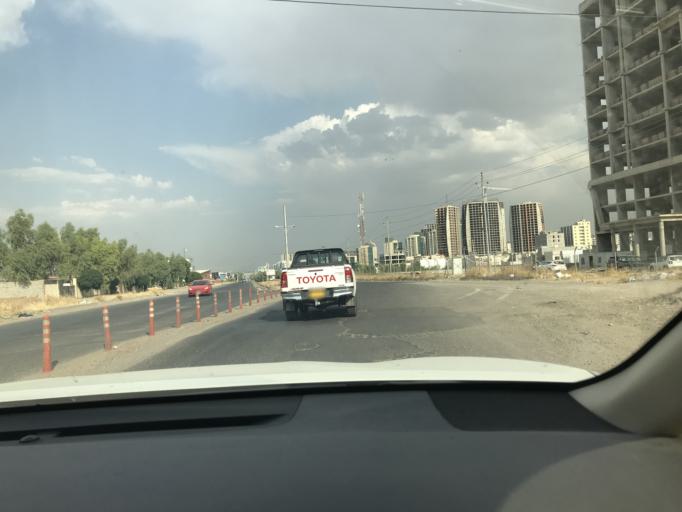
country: IQ
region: Arbil
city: Erbil
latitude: 36.2067
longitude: 43.9604
